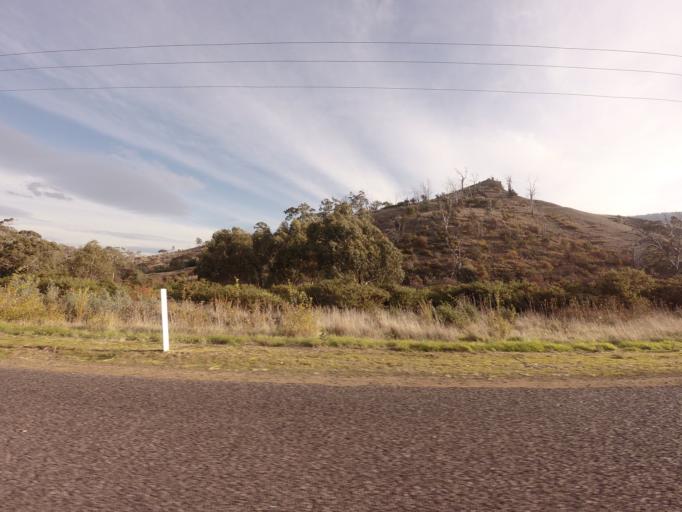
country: AU
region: Tasmania
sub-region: Brighton
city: Bridgewater
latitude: -42.4452
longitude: 147.1534
